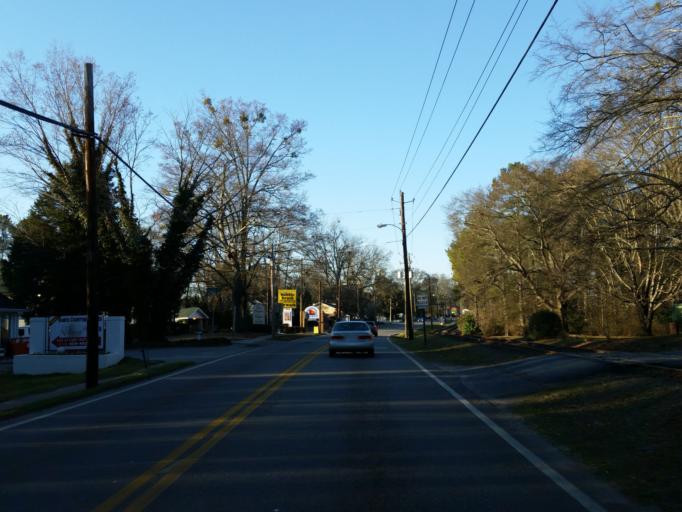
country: US
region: Georgia
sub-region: Cherokee County
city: Woodstock
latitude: 34.0946
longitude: -84.5203
